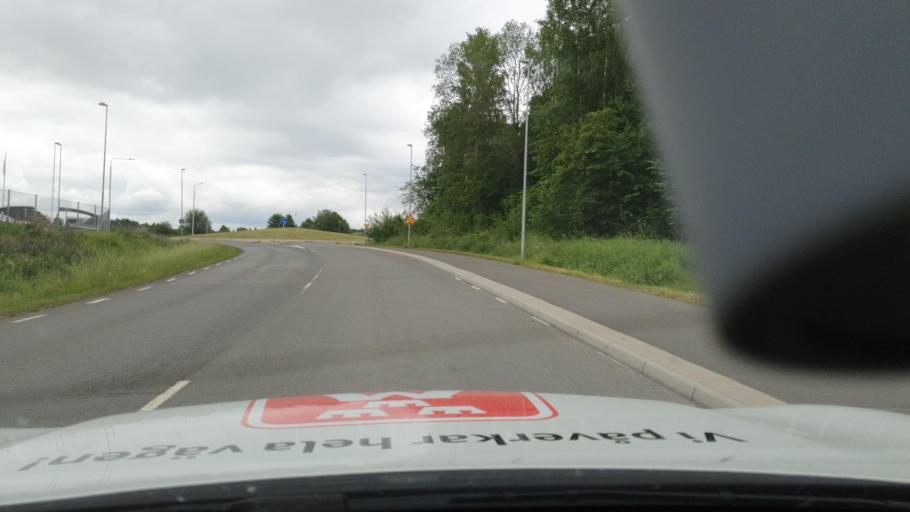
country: SE
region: Vaestra Goetaland
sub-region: Skovde Kommun
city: Skoevde
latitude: 58.3847
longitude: 13.8828
